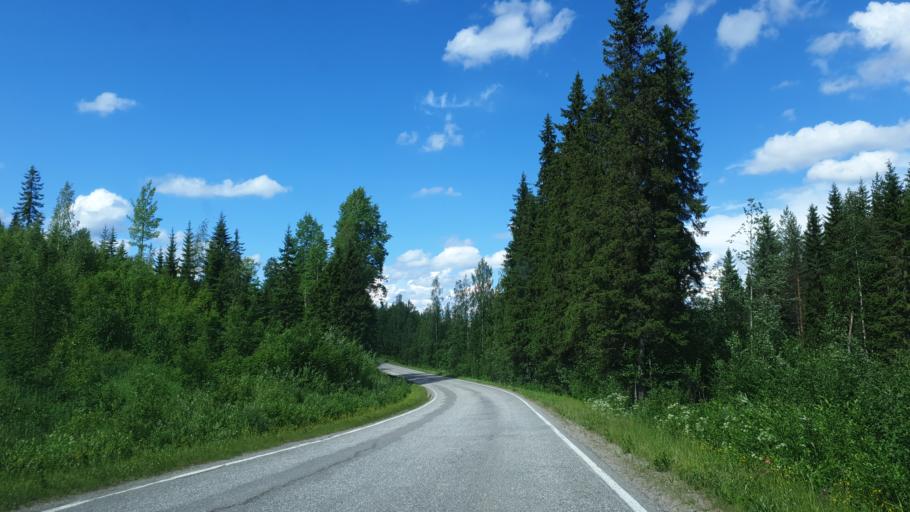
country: FI
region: Northern Savo
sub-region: Koillis-Savo
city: Kaavi
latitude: 63.0319
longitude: 28.6090
